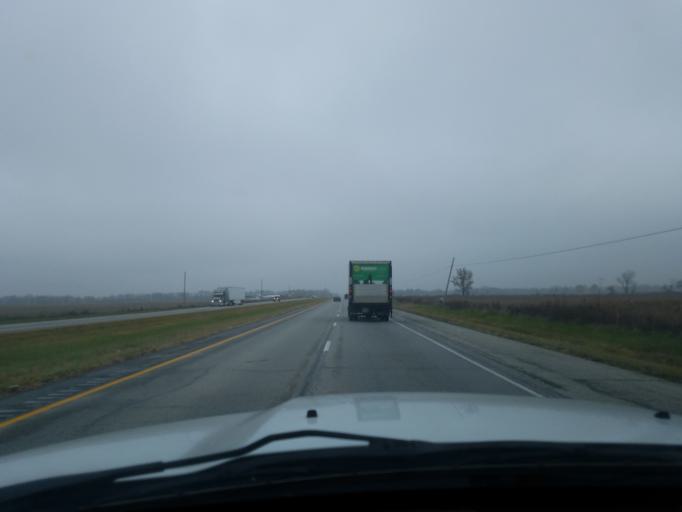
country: US
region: Indiana
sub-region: Hamilton County
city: Sheridan
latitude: 40.1798
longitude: -86.1278
